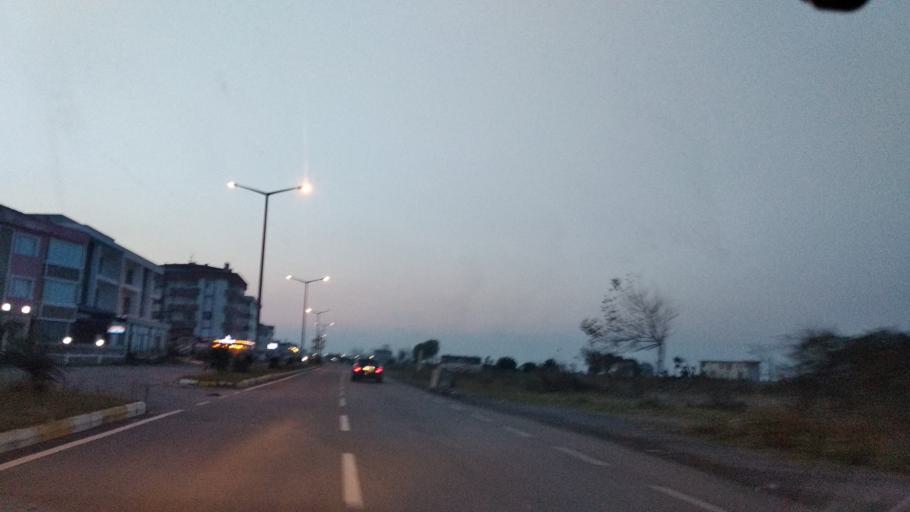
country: TR
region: Sakarya
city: Karasu
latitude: 41.0966
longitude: 30.7295
